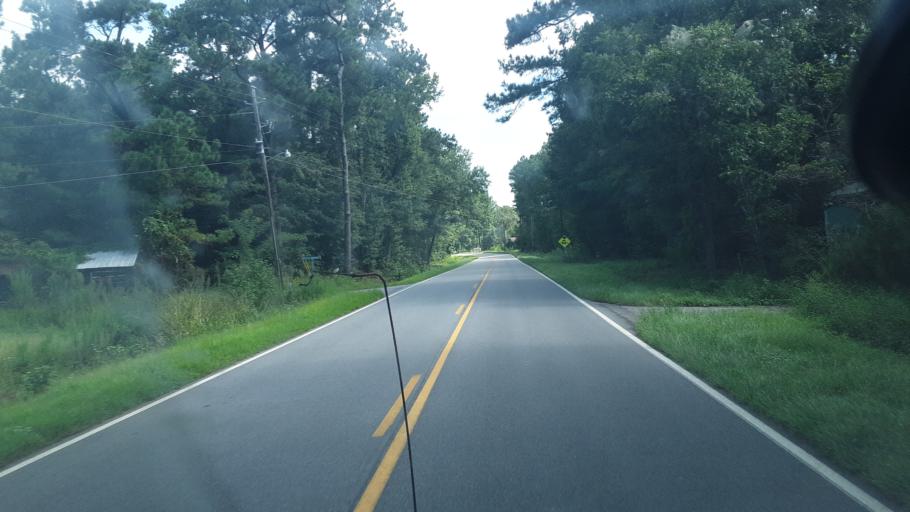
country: US
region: South Carolina
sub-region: Bamberg County
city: Bamberg
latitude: 33.0850
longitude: -81.0163
